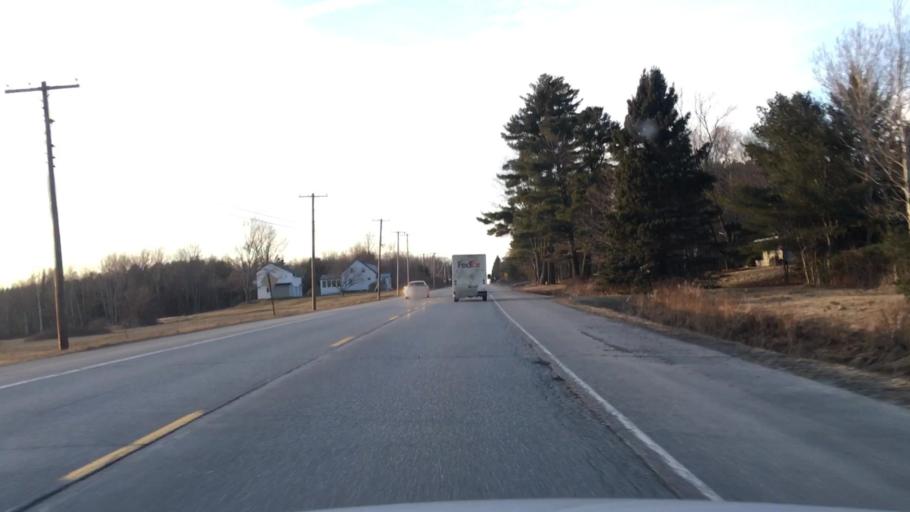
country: US
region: Maine
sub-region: Penobscot County
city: Holden
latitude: 44.7559
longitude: -68.6850
